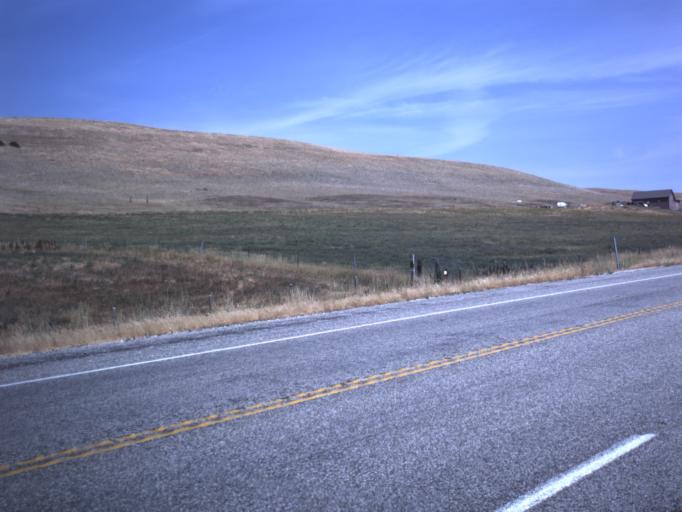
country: US
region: Utah
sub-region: Cache County
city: Mendon
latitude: 41.7934
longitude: -112.0351
